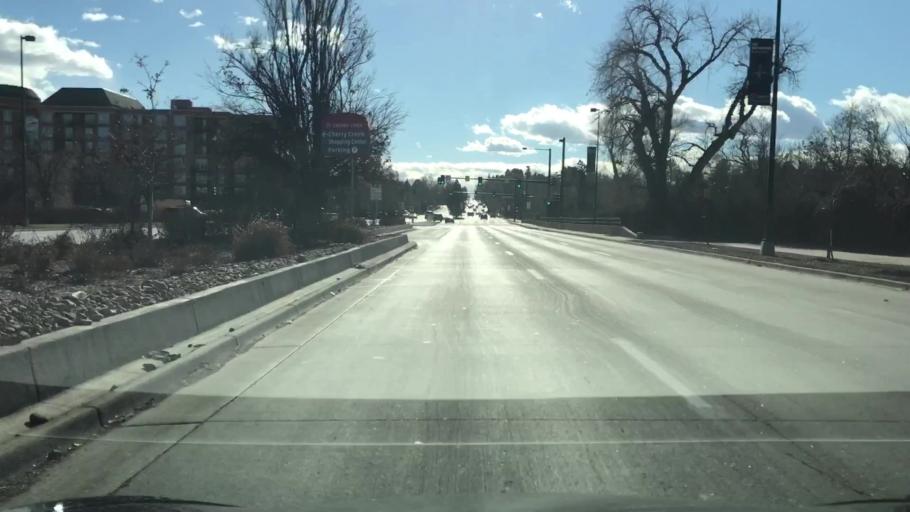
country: US
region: Colorado
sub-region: Arapahoe County
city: Glendale
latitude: 39.7172
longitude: -104.9593
